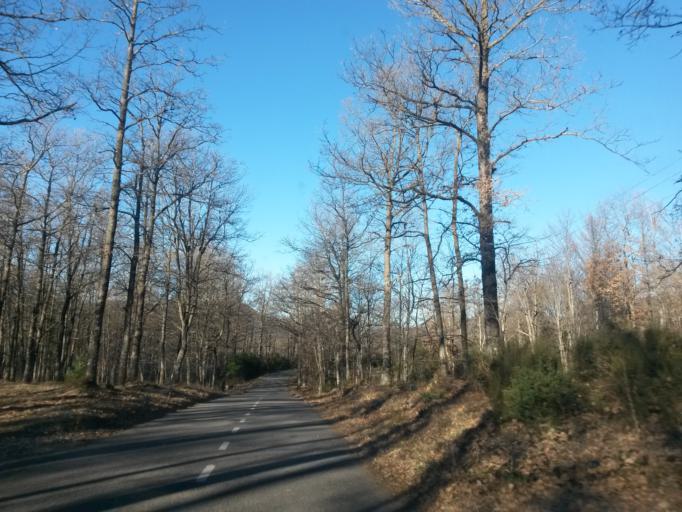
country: ES
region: Catalonia
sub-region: Provincia de Girona
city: les Planes d'Hostoles
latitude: 42.0300
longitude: 2.5238
